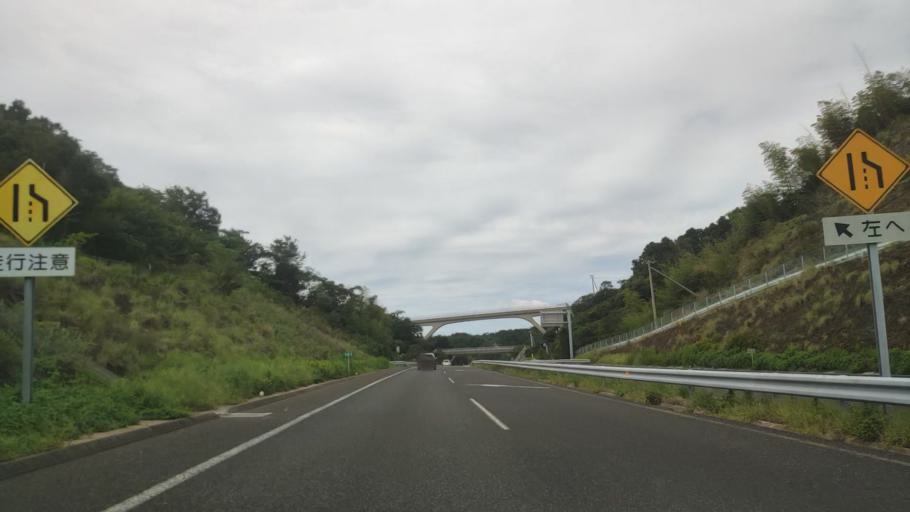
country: JP
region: Wakayama
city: Gobo
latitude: 33.8128
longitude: 135.2330
